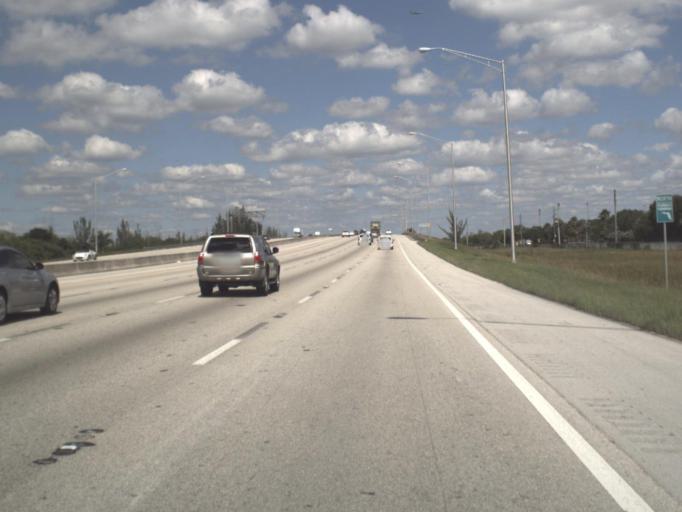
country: US
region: Florida
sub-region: Miami-Dade County
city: Doral
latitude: 25.8222
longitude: -80.3865
